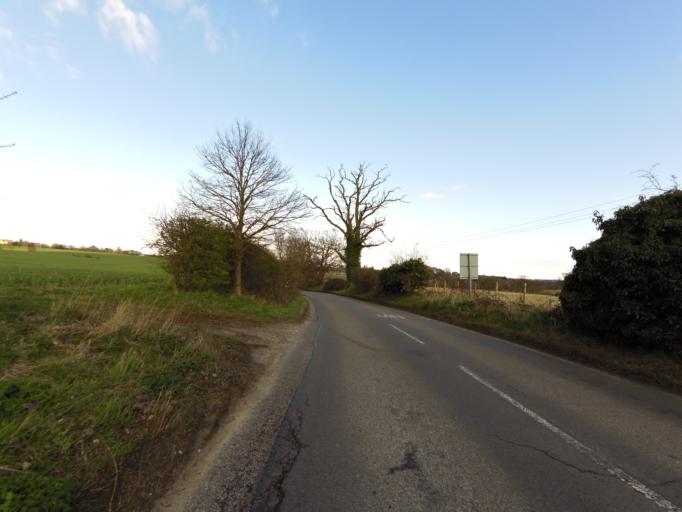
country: GB
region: England
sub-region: Suffolk
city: Kesgrave
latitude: 52.0919
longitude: 1.2161
